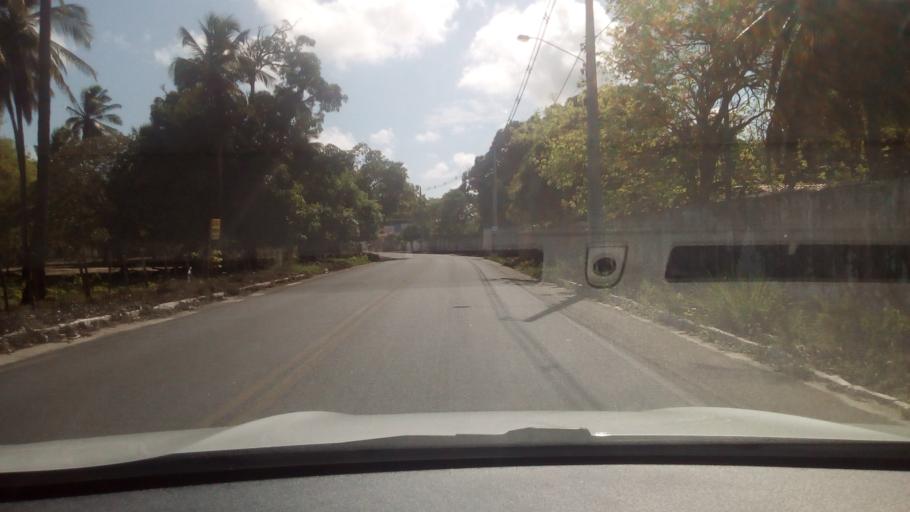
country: BR
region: Paraiba
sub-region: Conde
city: Conde
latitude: -7.2074
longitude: -34.8271
